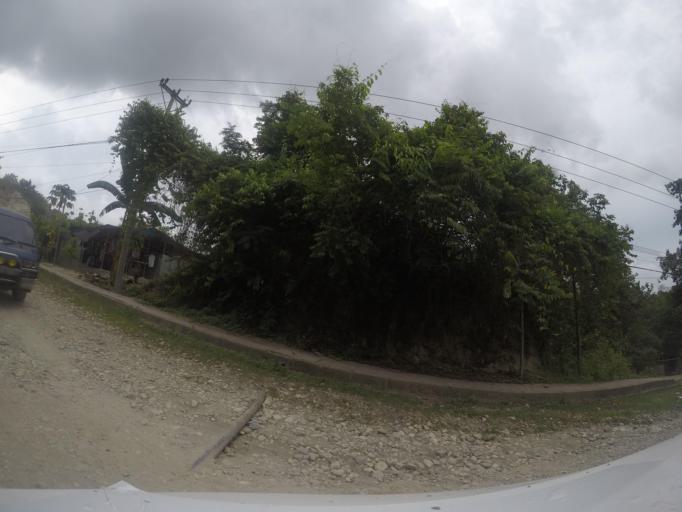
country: TL
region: Viqueque
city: Viqueque
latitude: -8.8632
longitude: 126.3625
